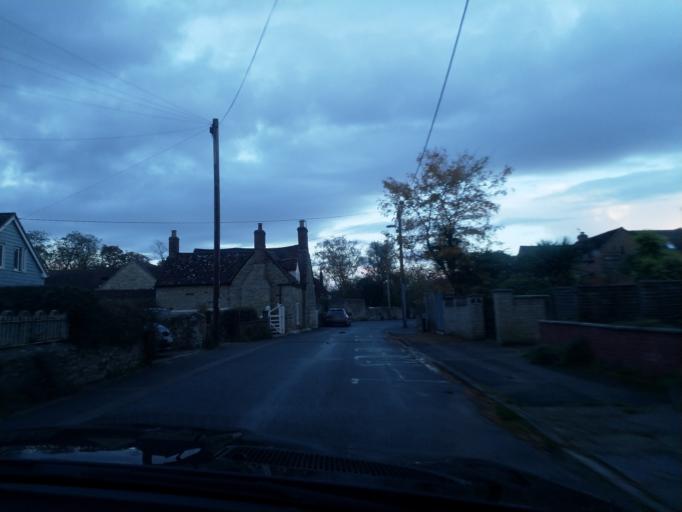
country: GB
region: England
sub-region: Oxfordshire
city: Wheatley
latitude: 51.7455
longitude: -1.1325
